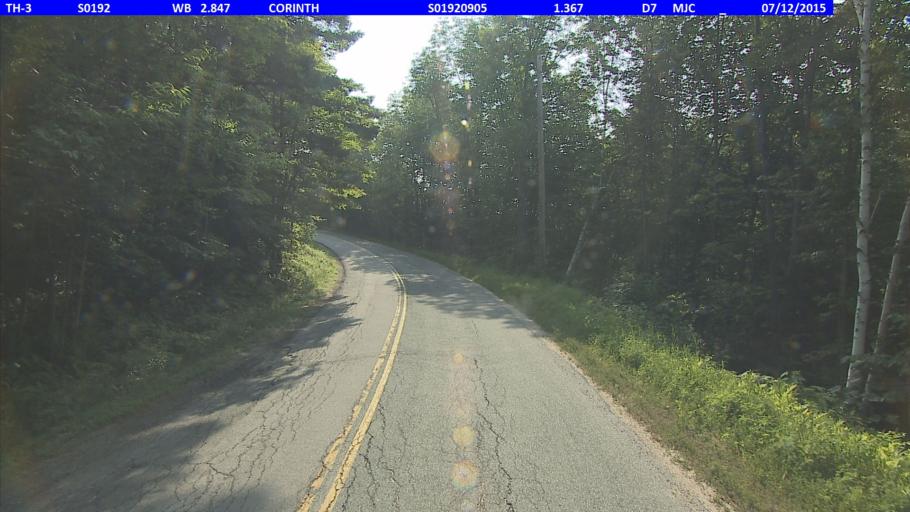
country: US
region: Vermont
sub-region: Orange County
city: Chelsea
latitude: 44.0064
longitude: -72.3308
